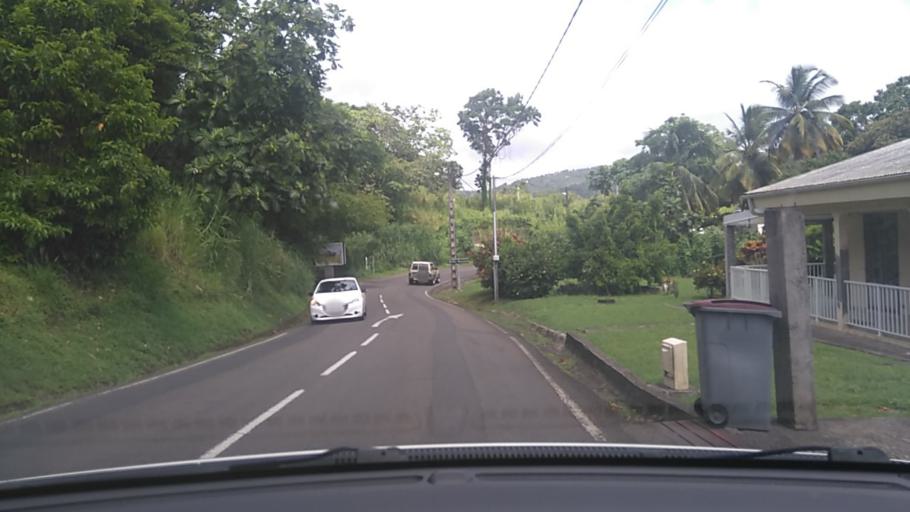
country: MQ
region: Martinique
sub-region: Martinique
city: Saint-Esprit
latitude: 14.5598
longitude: -60.9320
